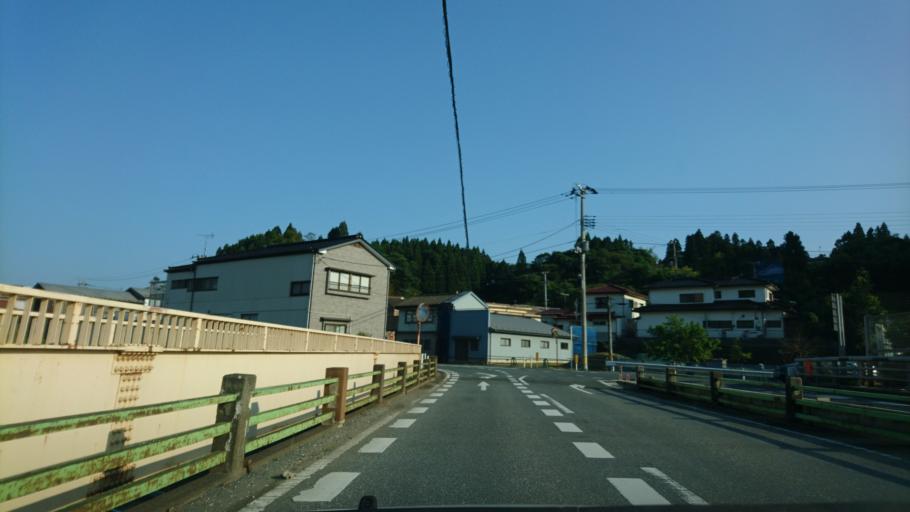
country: JP
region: Iwate
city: Ofunato
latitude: 38.9116
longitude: 141.5550
